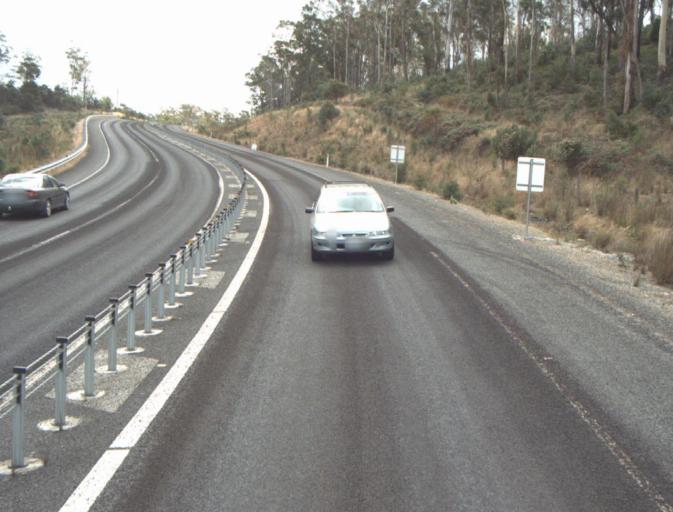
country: AU
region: Tasmania
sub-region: Launceston
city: Mayfield
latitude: -41.2920
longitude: 147.0471
